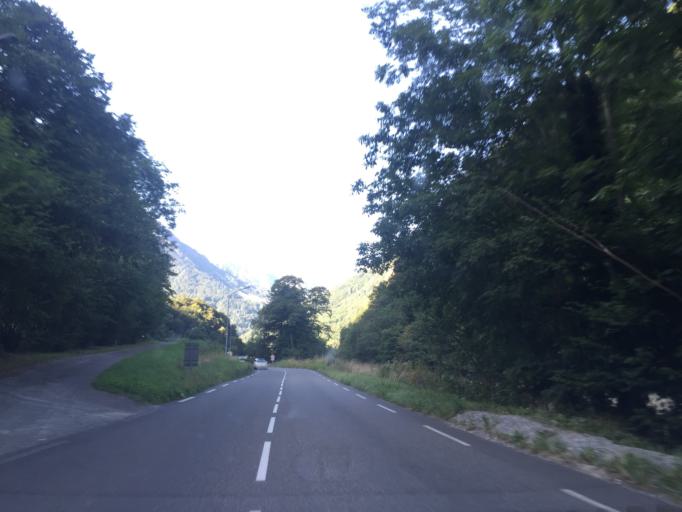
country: FR
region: Midi-Pyrenees
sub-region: Departement des Hautes-Pyrenees
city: Cauterets
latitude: 42.9101
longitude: -0.0999
